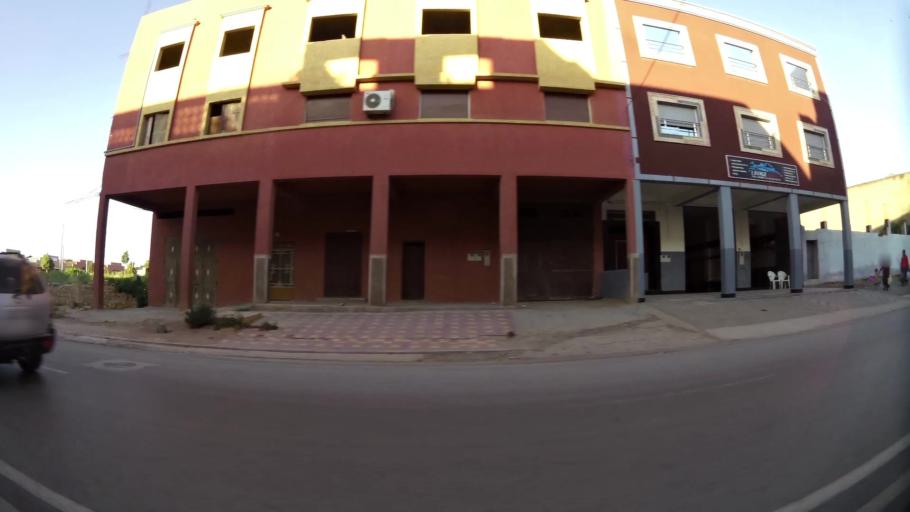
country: MA
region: Oriental
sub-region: Berkane-Taourirt
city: Berkane
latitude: 34.9253
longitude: -2.3183
